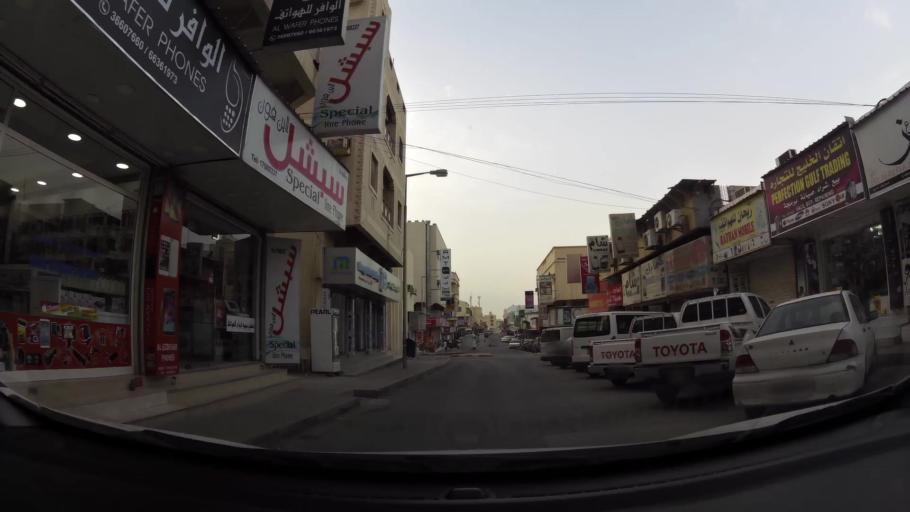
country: BH
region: Northern
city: Ar Rifa'
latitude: 26.1215
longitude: 50.5677
